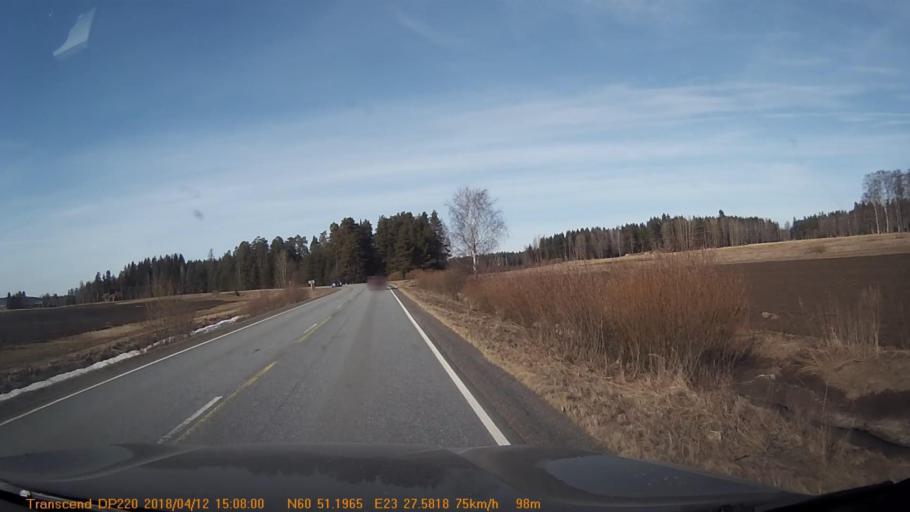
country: FI
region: Haeme
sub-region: Forssa
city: Jokioinen
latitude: 60.8537
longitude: 23.4596
